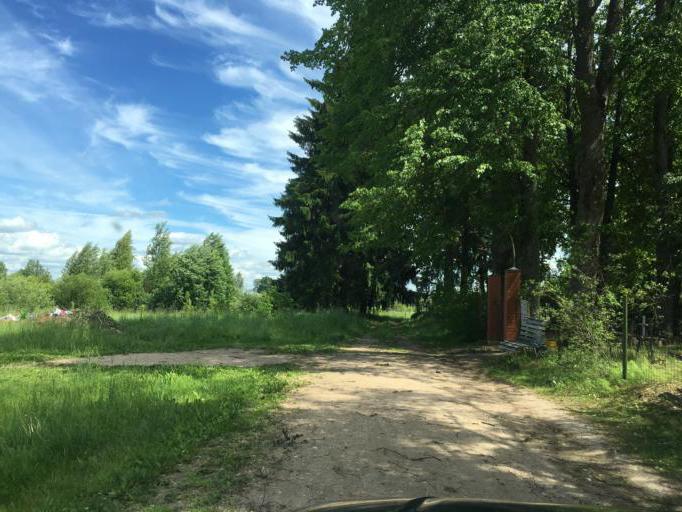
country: LV
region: Balvu Rajons
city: Balvi
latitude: 57.1555
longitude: 27.3205
